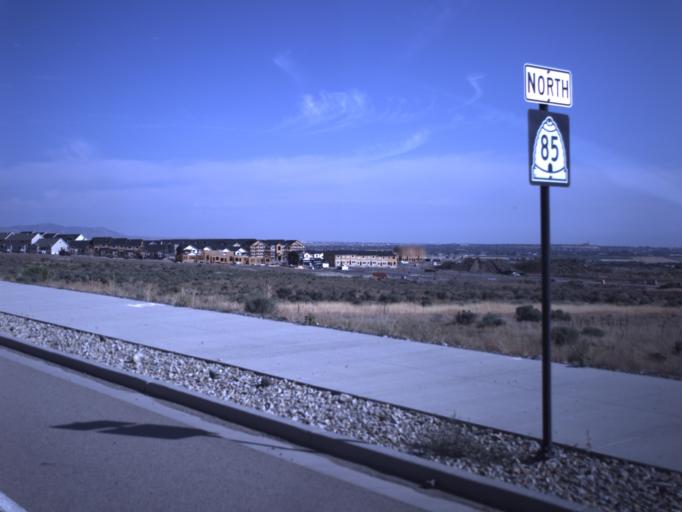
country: US
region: Utah
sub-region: Salt Lake County
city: Bluffdale
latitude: 40.4829
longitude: -111.9890
